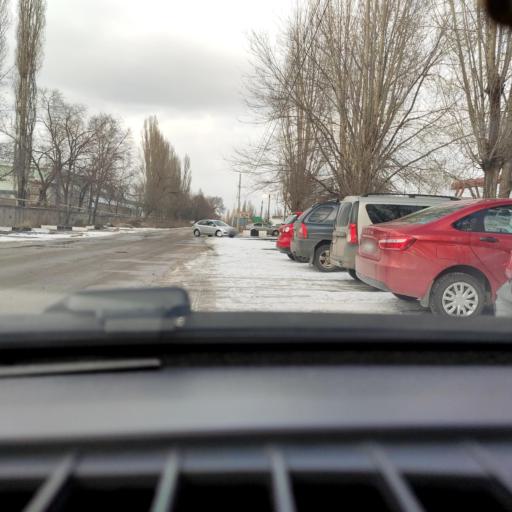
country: RU
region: Voronezj
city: Maslovka
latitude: 51.6448
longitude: 39.2858
